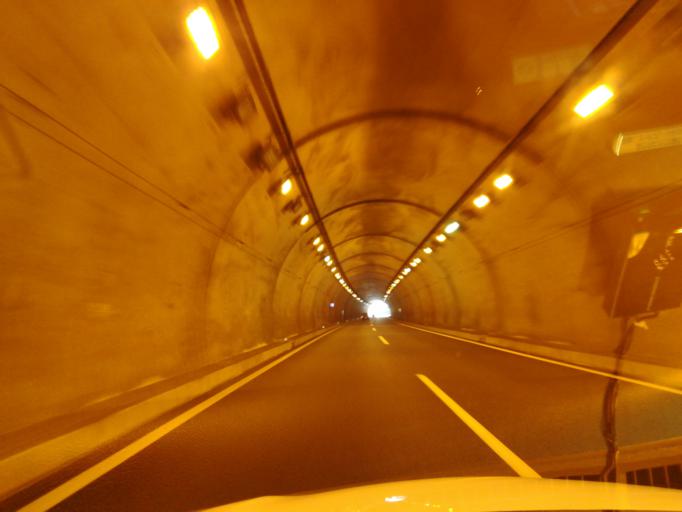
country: JP
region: Ehime
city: Kawanoecho
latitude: 33.8005
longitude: 133.6610
